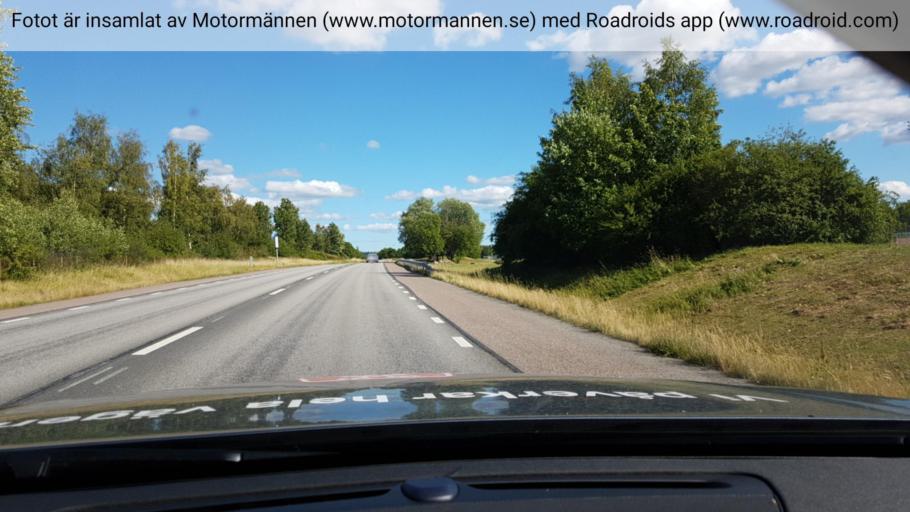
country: SE
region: Stockholm
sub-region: Sigtuna Kommun
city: Marsta
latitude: 59.6231
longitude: 17.8342
